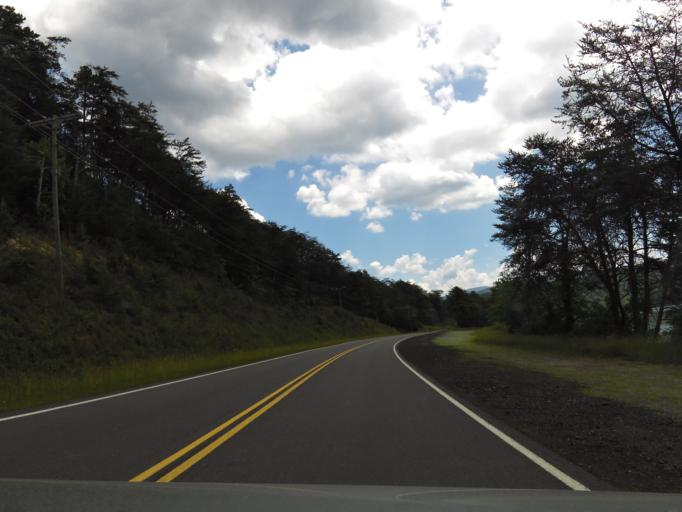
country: US
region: Tennessee
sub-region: Loudon County
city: Greenback
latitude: 35.5513
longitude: -84.0274
